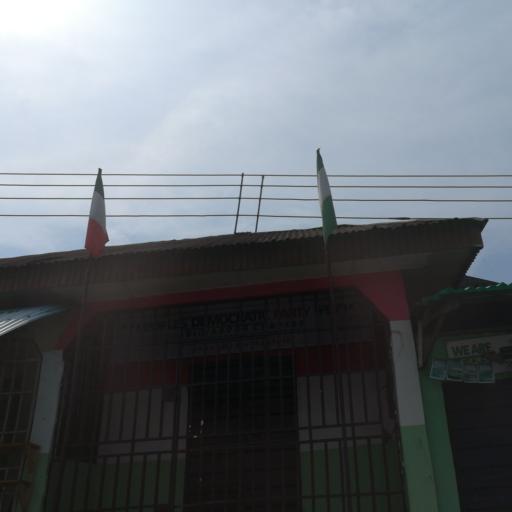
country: NG
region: Rivers
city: Port Harcourt
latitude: 4.8652
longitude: 7.0222
